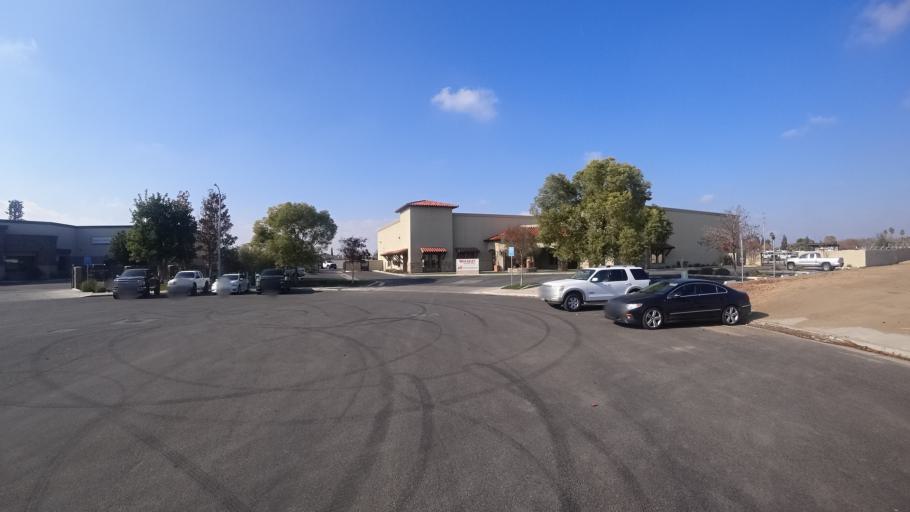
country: US
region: California
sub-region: Kern County
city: Greenacres
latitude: 35.3084
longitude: -119.0998
